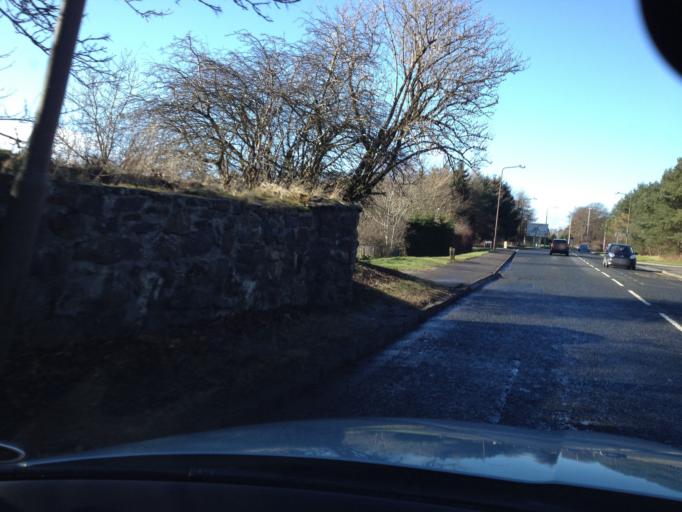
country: GB
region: Scotland
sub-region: West Lothian
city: Livingston
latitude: 55.8868
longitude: -3.5473
